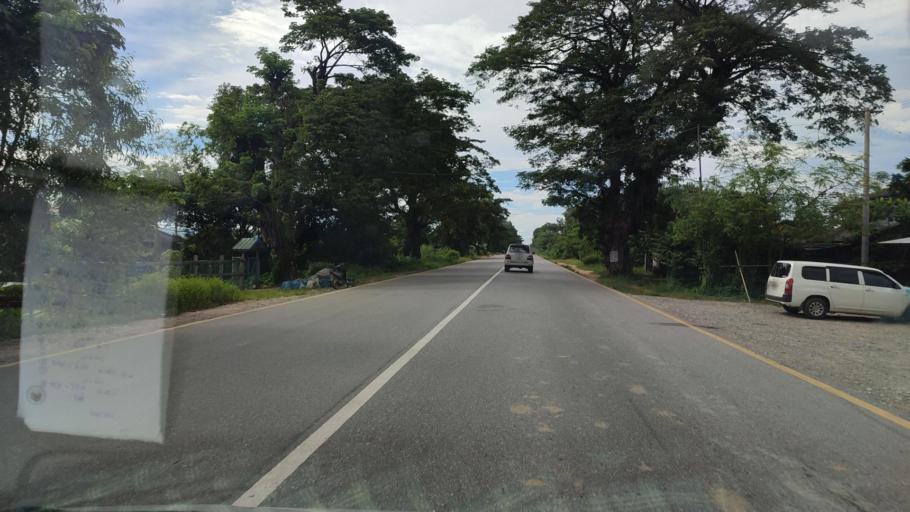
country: MM
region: Bago
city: Pyu
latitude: 18.3933
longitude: 96.4664
